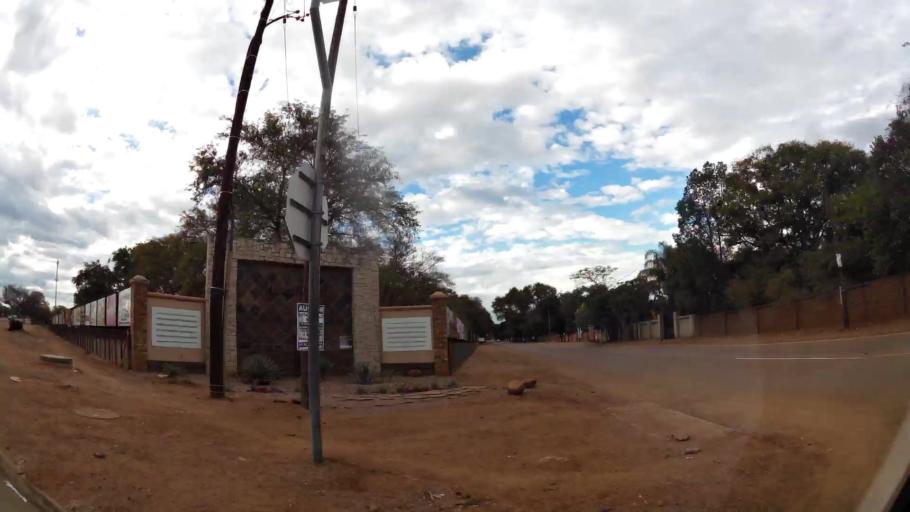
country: ZA
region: Limpopo
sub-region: Waterberg District Municipality
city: Modimolle
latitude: -24.5148
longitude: 28.7069
